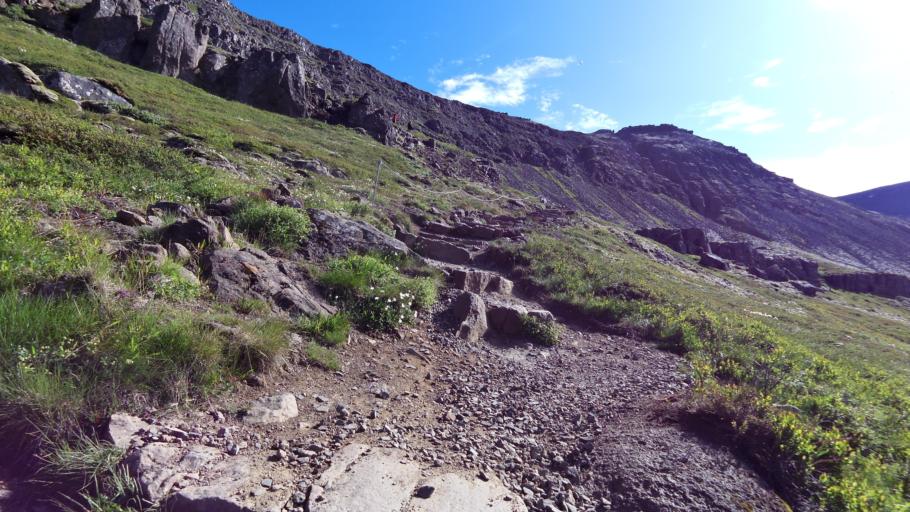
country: IS
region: Westfjords
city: Isafjoerdur
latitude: 65.7330
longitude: -23.2040
